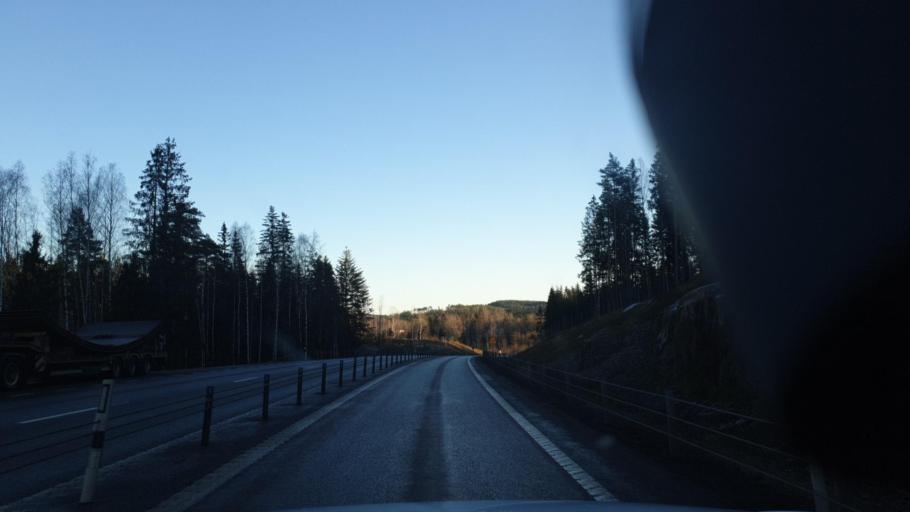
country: SE
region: Vaermland
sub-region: Arvika Kommun
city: Arvika
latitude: 59.6611
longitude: 12.7686
